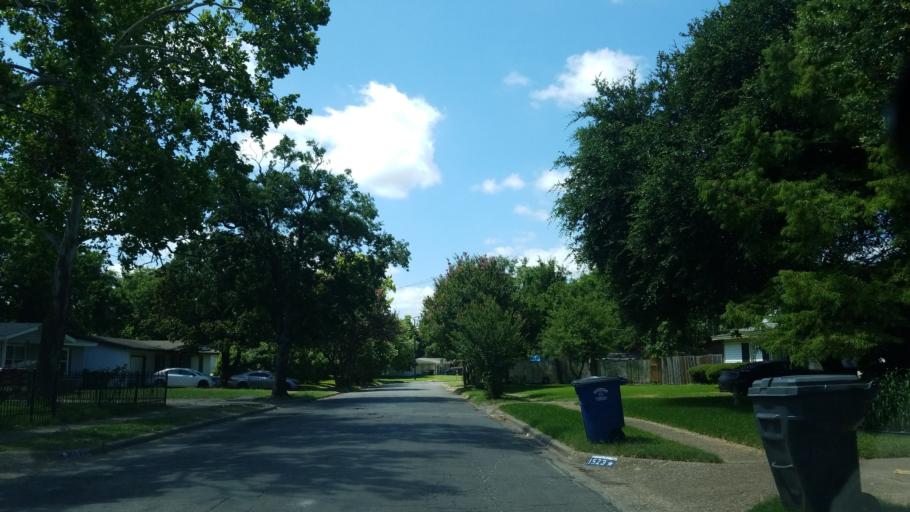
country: US
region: Texas
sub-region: Dallas County
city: Balch Springs
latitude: 32.7390
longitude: -96.6939
